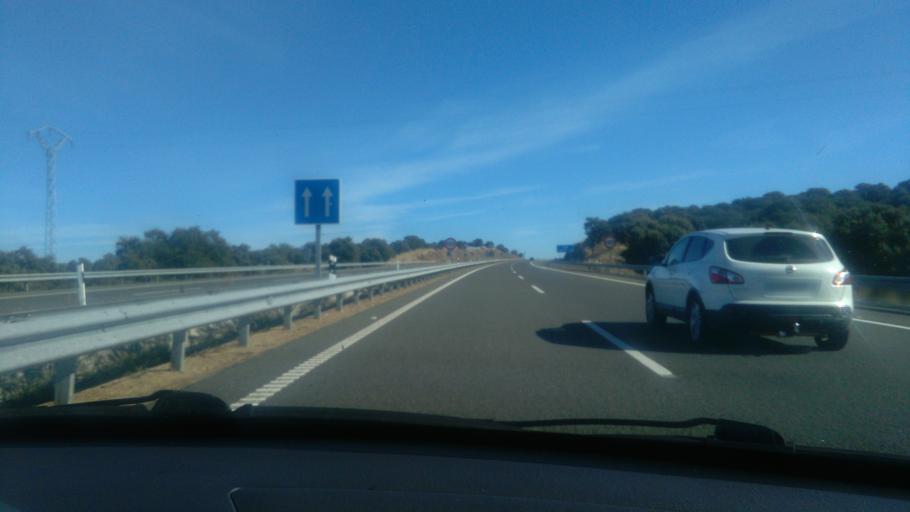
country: ES
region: Extremadura
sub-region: Provincia de Caceres
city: Plasenzuela
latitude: 39.4422
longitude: -6.0501
